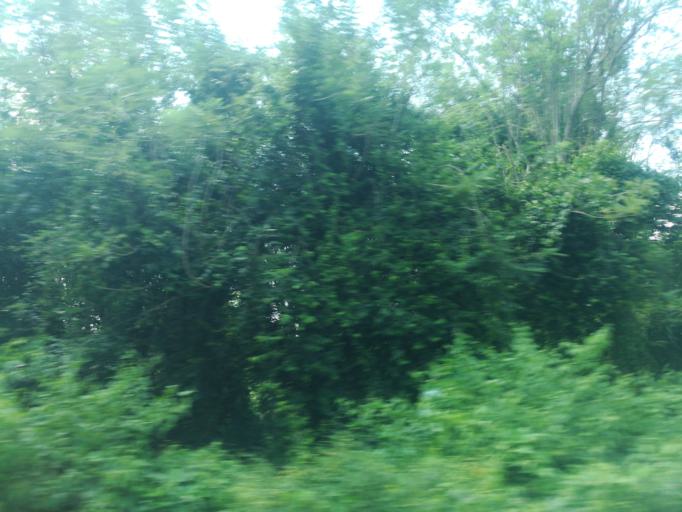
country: NG
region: Oyo
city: Moniya
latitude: 7.5598
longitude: 3.9097
